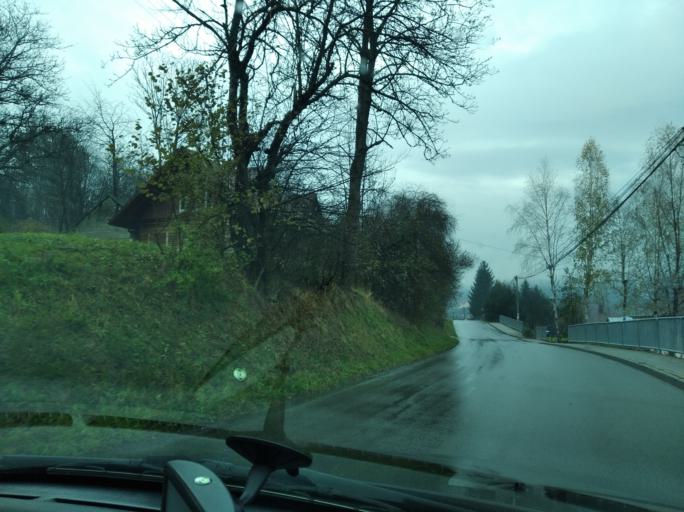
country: PL
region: Subcarpathian Voivodeship
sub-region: Powiat rzeszowski
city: Lubenia
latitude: 49.9274
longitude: 21.9303
